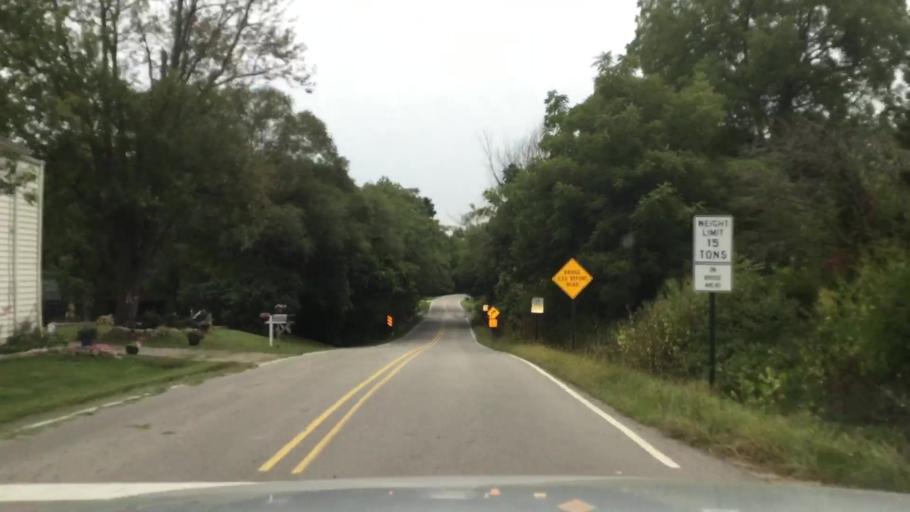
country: US
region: Michigan
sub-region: Washtenaw County
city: Milan
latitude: 42.1030
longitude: -83.7336
